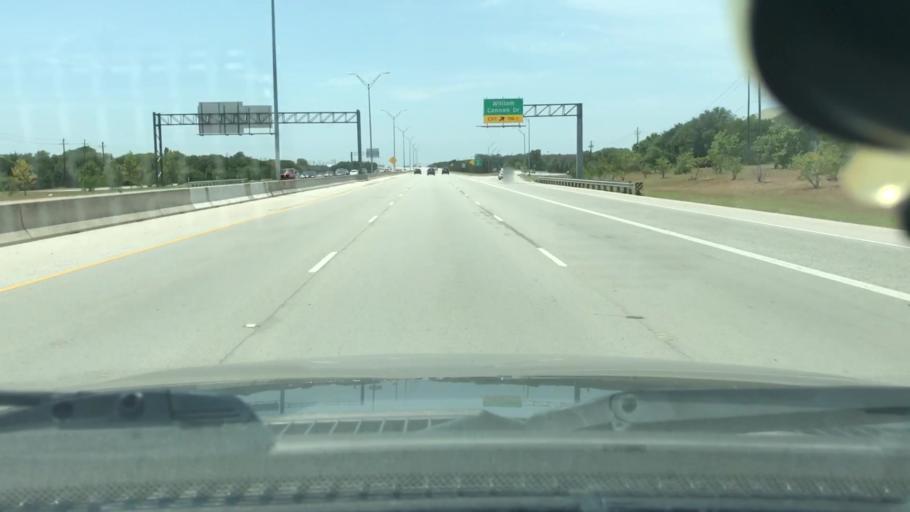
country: US
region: Texas
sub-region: Travis County
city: Rollingwood
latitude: 30.2274
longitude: -97.8303
